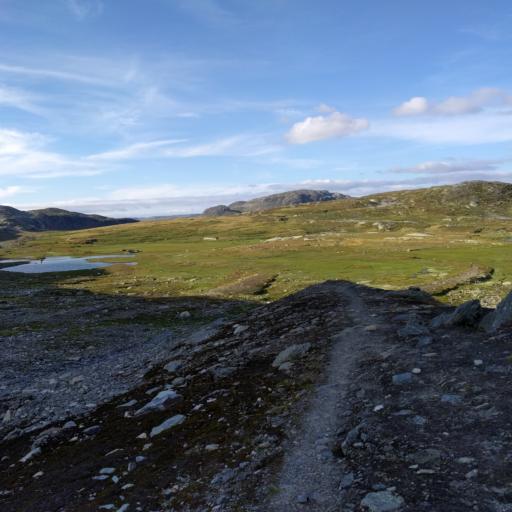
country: NO
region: Aust-Agder
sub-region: Bykle
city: Hovden
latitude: 59.9292
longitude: 7.2163
